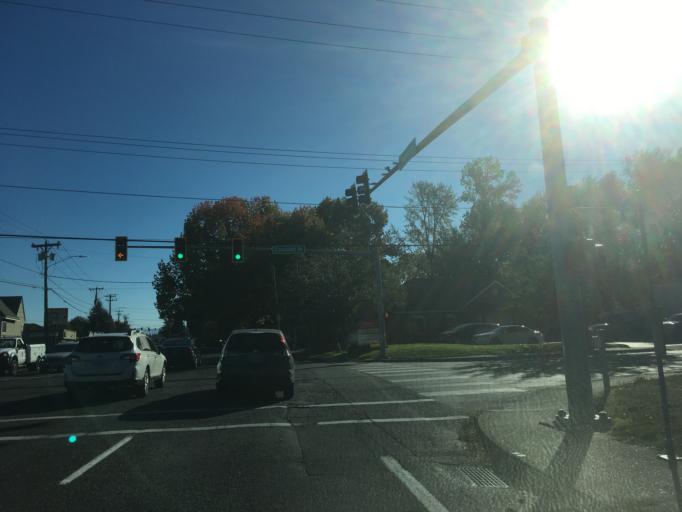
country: US
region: Oregon
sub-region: Multnomah County
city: Gresham
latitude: 45.5048
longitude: -122.4214
